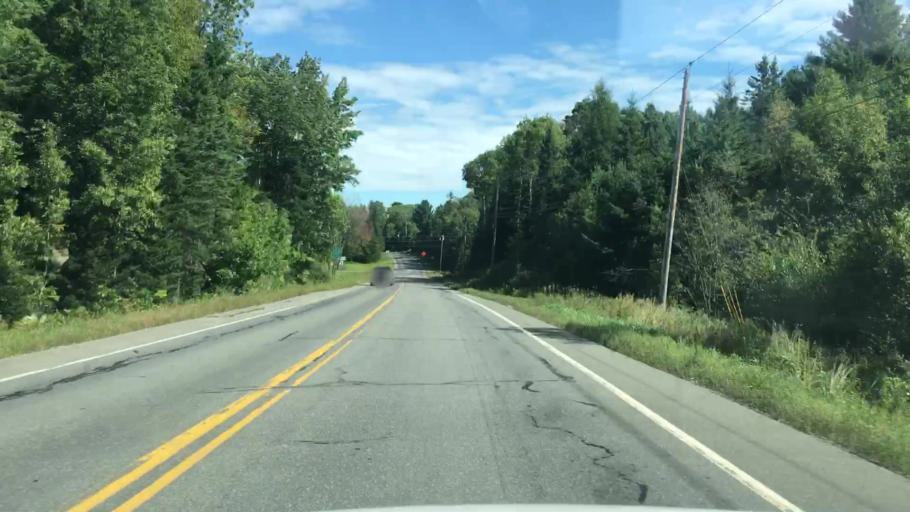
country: US
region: Maine
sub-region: Penobscot County
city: Garland
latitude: 45.0922
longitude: -69.2134
